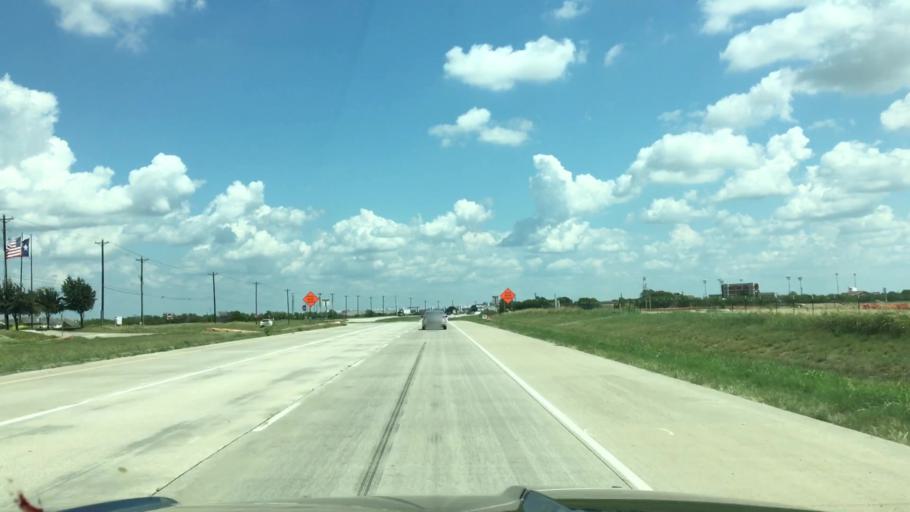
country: US
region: Texas
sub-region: Denton County
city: Justin
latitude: 33.0351
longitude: -97.3311
